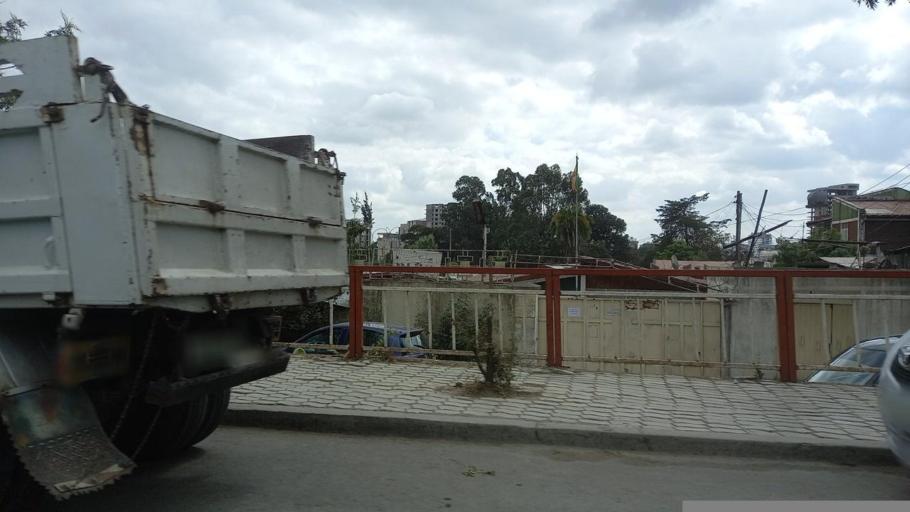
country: ET
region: Adis Abeba
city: Addis Ababa
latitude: 9.0214
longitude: 38.7906
